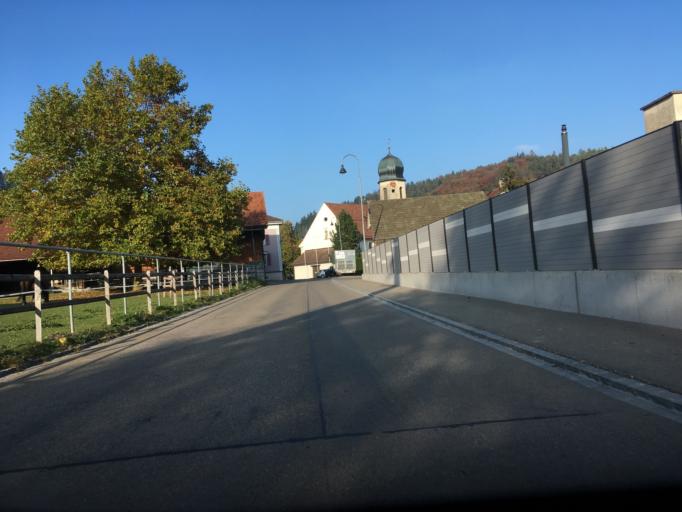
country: CH
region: Saint Gallen
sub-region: Wahlkreis Toggenburg
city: Mosnang
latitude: 47.3613
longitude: 9.0385
